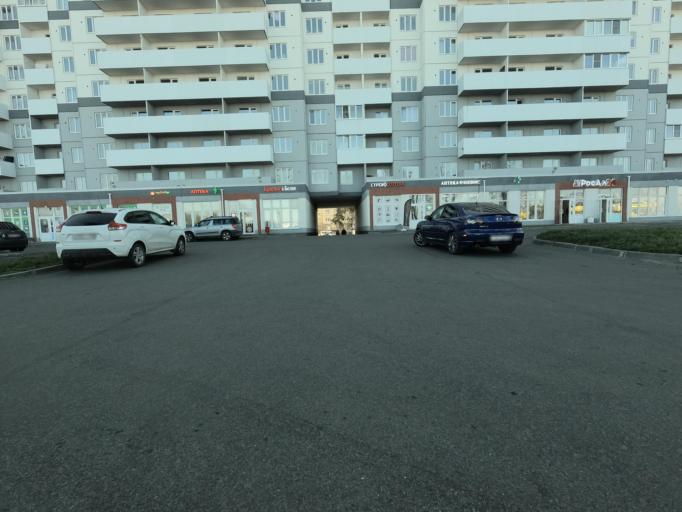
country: RU
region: St.-Petersburg
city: Petro-Slavyanka
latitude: 59.7617
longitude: 30.4714
